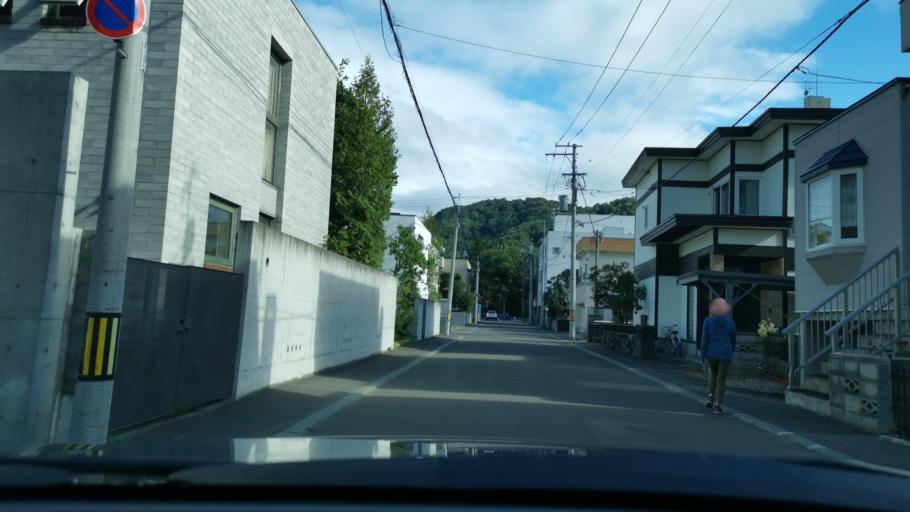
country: JP
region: Hokkaido
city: Sapporo
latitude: 43.0587
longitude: 141.3129
